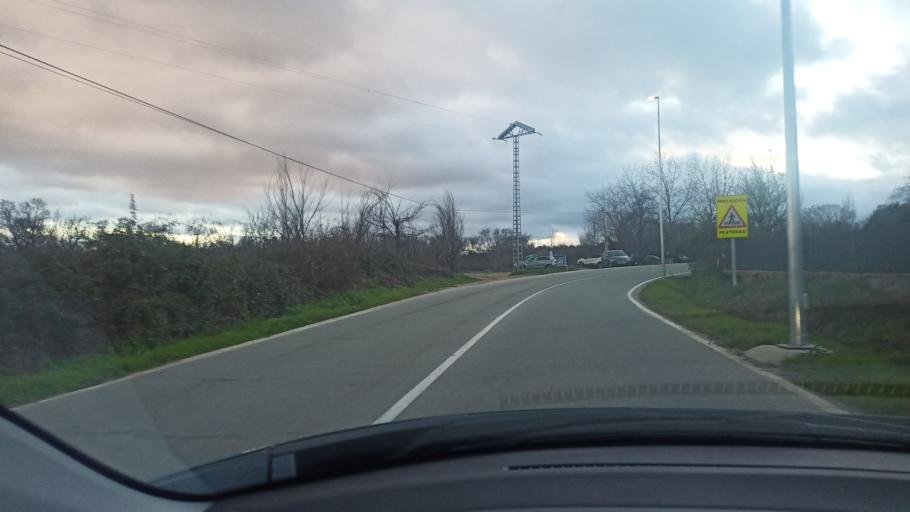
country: ES
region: Madrid
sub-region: Provincia de Madrid
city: El Escorial
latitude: 40.5391
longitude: -4.1241
